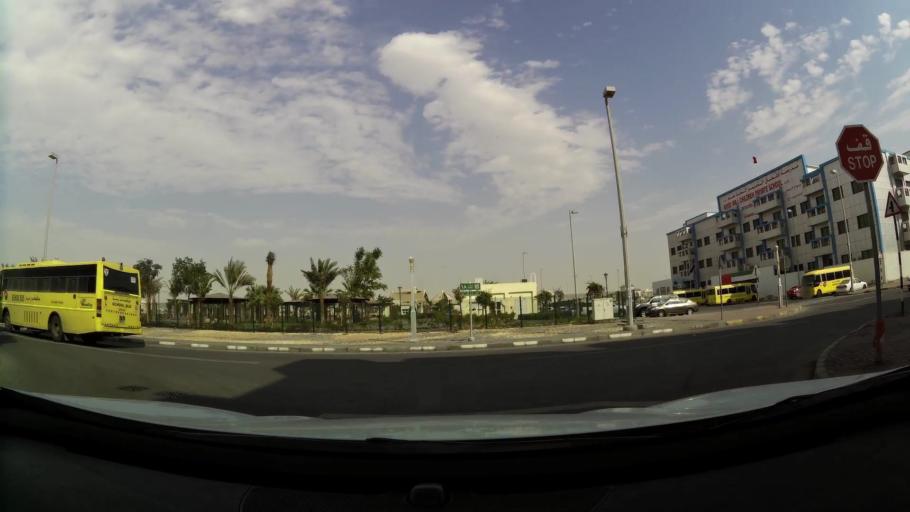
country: AE
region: Abu Dhabi
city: Abu Dhabi
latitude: 24.3308
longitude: 54.5367
